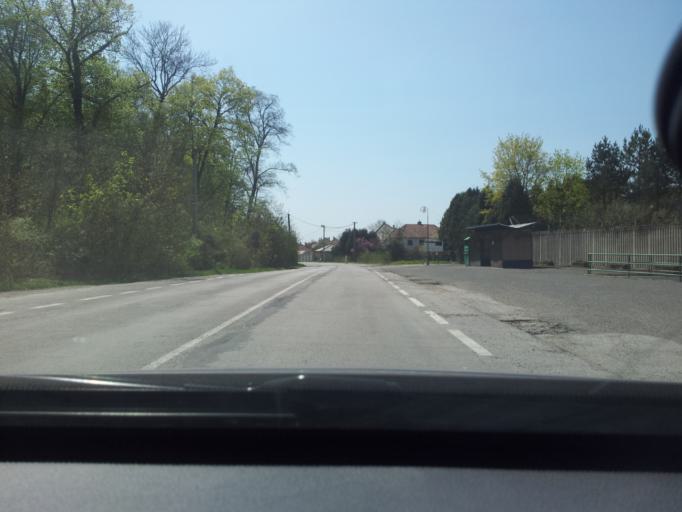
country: SK
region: Nitriansky
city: Zlate Moravce
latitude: 48.4324
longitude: 18.4113
